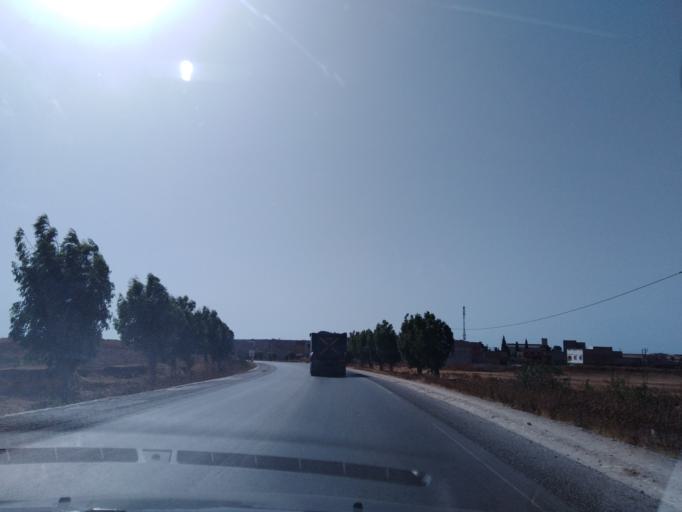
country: MA
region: Doukkala-Abda
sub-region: Safi
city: Safi
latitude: 32.2529
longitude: -8.9757
